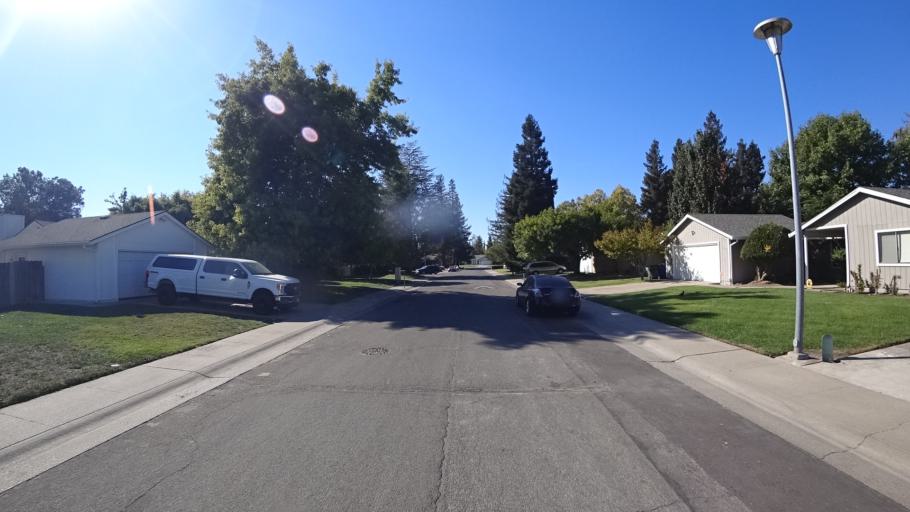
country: US
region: California
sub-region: Sacramento County
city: Parkway
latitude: 38.4914
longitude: -121.5370
